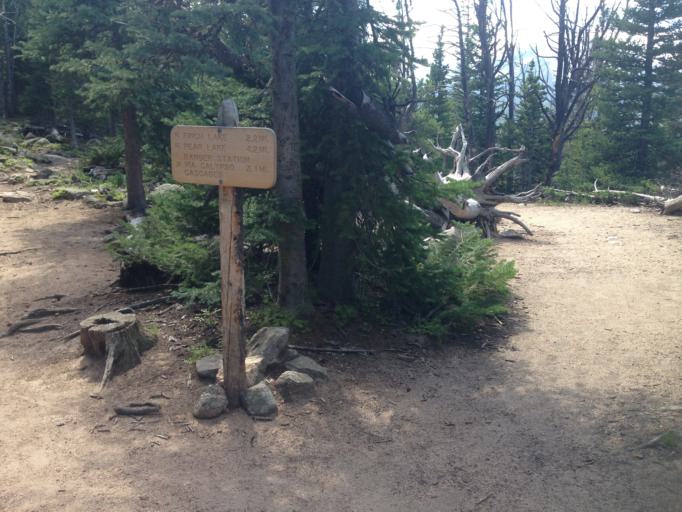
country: US
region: Colorado
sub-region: Larimer County
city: Estes Park
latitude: 40.1996
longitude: -105.5704
